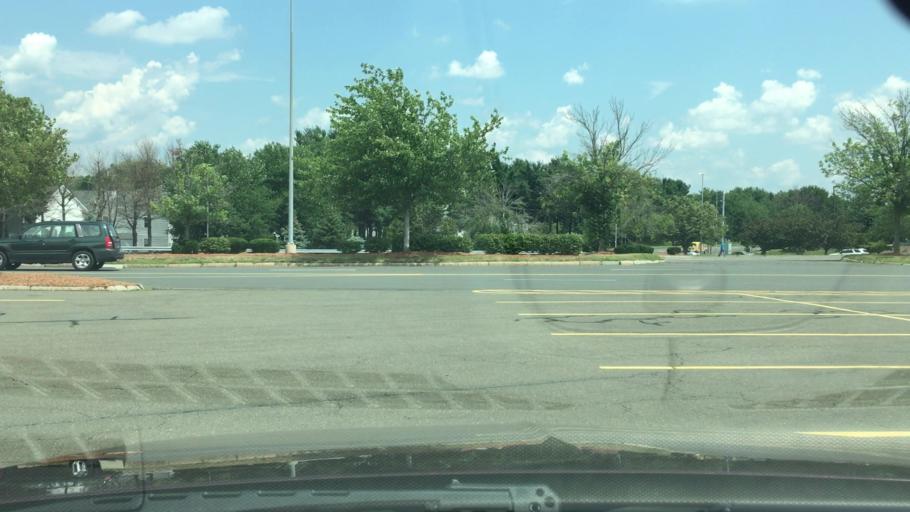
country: US
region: Connecticut
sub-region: Hartford County
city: Manchester
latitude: 41.8076
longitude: -72.5426
